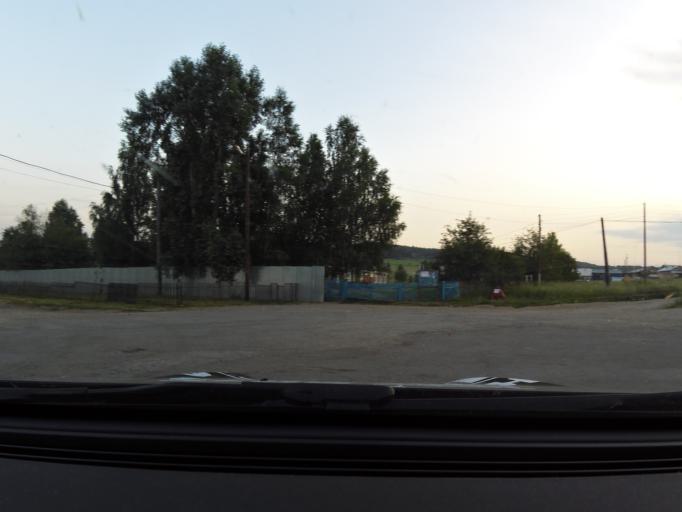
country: RU
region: Sverdlovsk
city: Arti
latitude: 56.3706
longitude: 58.5656
